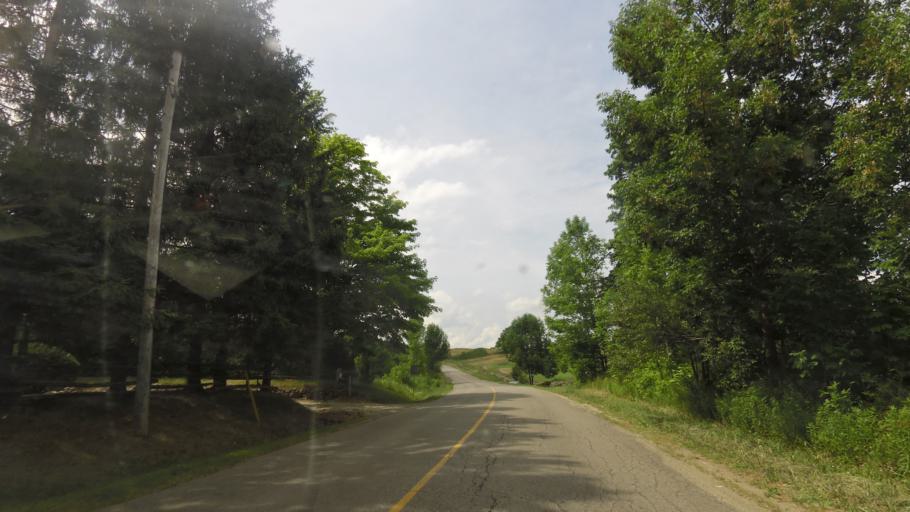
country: CA
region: Ontario
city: Orangeville
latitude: 43.8728
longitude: -79.9125
